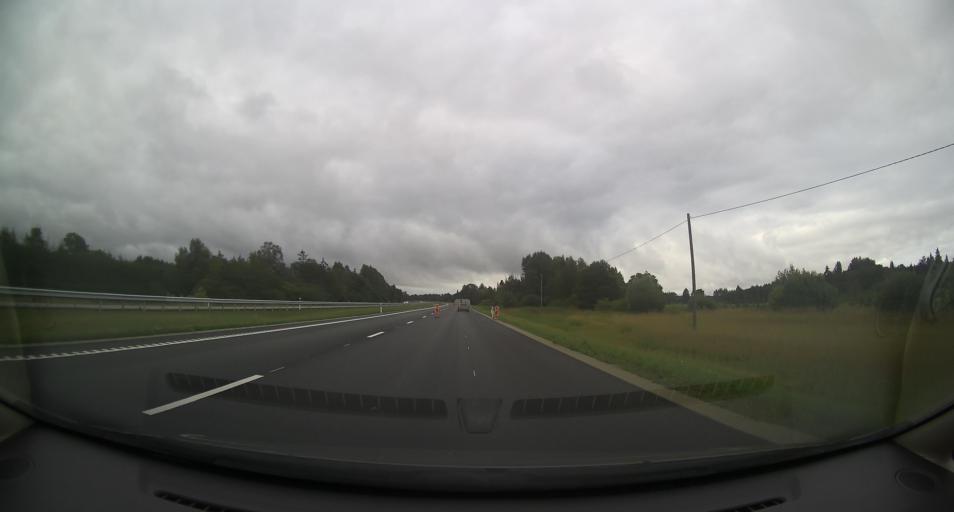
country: EE
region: Harju
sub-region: Rae vald
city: Vaida
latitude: 59.3066
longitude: 24.9476
